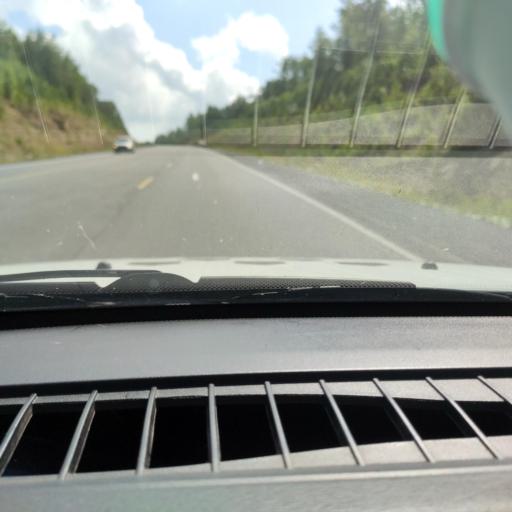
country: RU
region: Chelyabinsk
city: Mezhevoy
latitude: 55.0956
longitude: 58.8763
